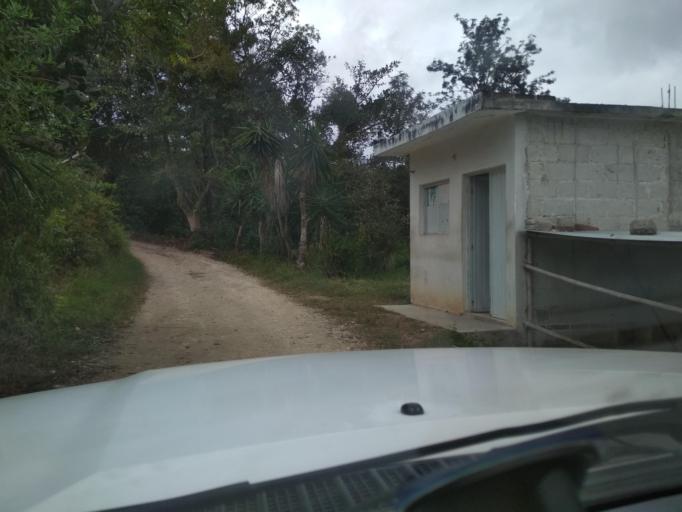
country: MX
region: Veracruz
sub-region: Emiliano Zapata
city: Dos Rios
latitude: 19.5392
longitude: -96.8002
